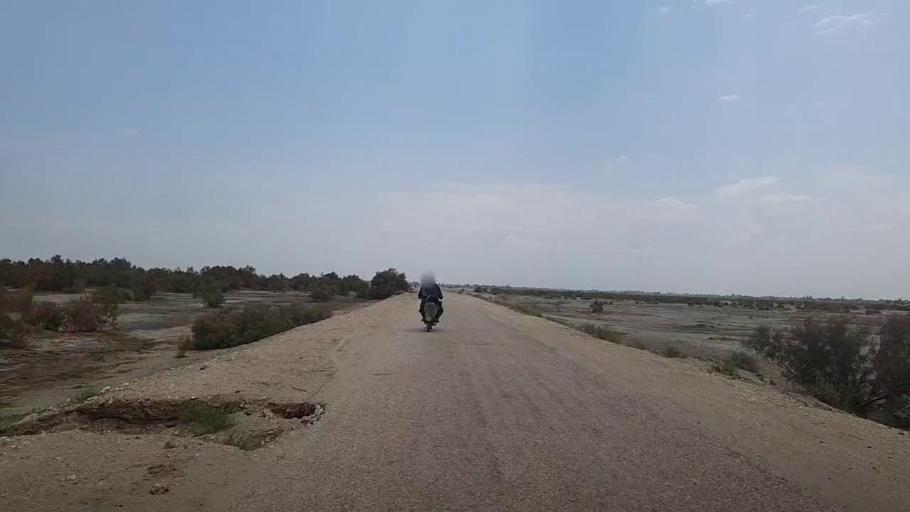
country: PK
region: Sindh
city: Kandhkot
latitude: 28.2881
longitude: 69.1496
